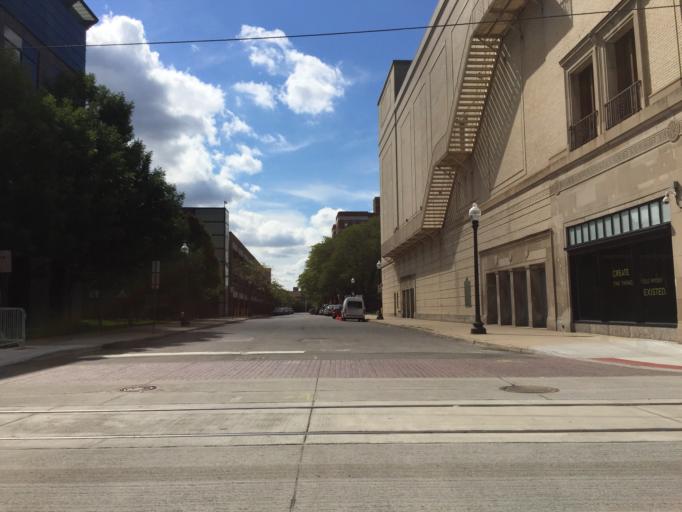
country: US
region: Michigan
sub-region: Wayne County
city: Detroit
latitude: 42.3486
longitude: -83.0588
